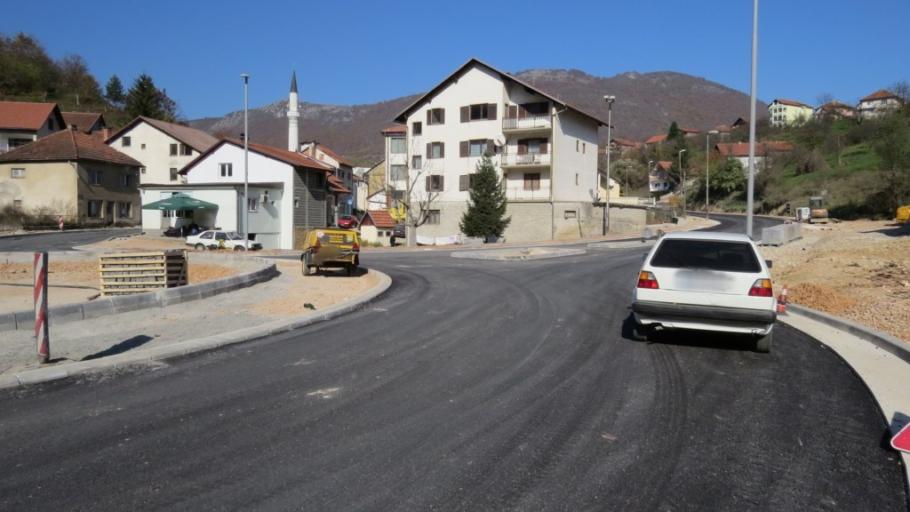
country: BA
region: Federation of Bosnia and Herzegovina
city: Prozor
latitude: 43.8166
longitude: 17.6133
